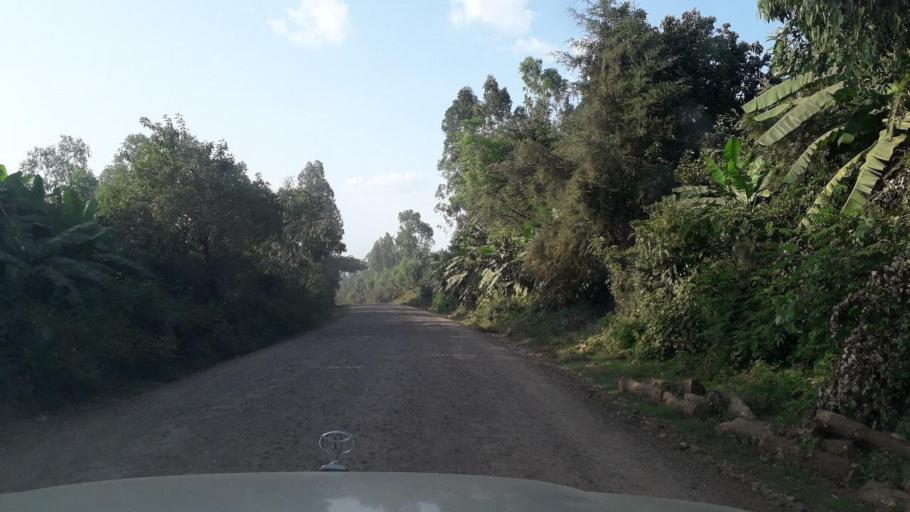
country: ET
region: Oromiya
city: Jima
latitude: 7.5708
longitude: 36.8604
